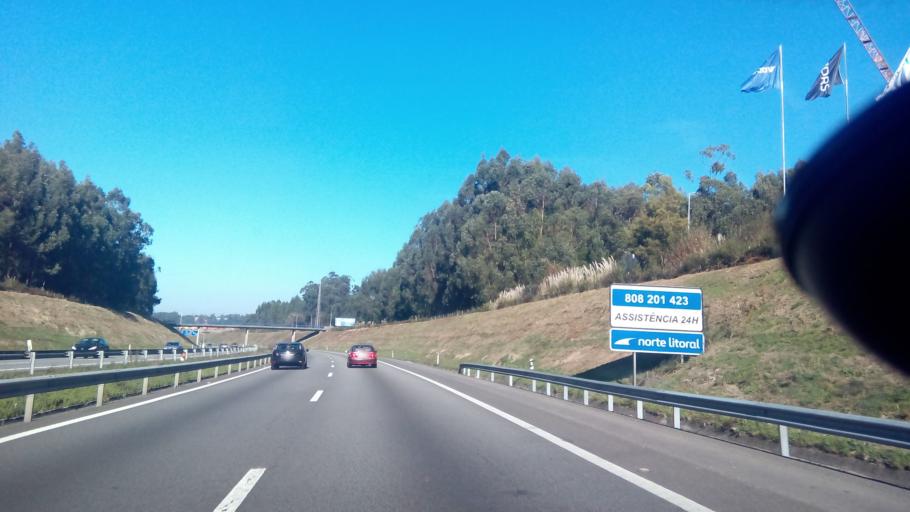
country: PT
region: Porto
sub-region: Matosinhos
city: Santa Cruz do Bispo
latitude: 41.2443
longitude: -8.6942
